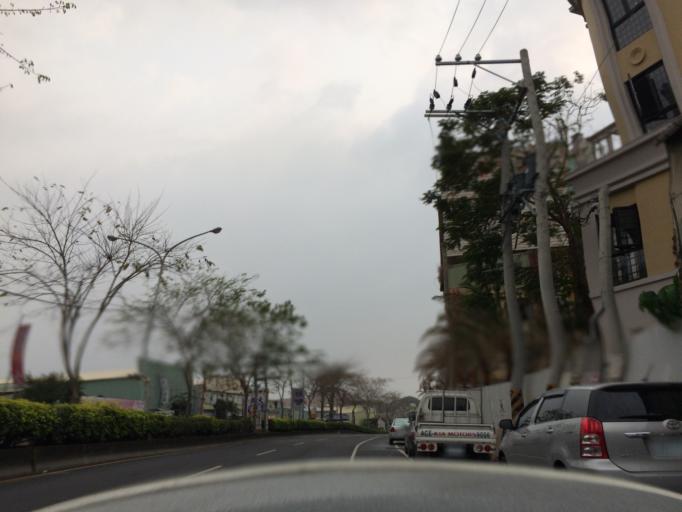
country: TW
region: Taiwan
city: Zhongxing New Village
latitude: 24.0045
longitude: 120.6944
